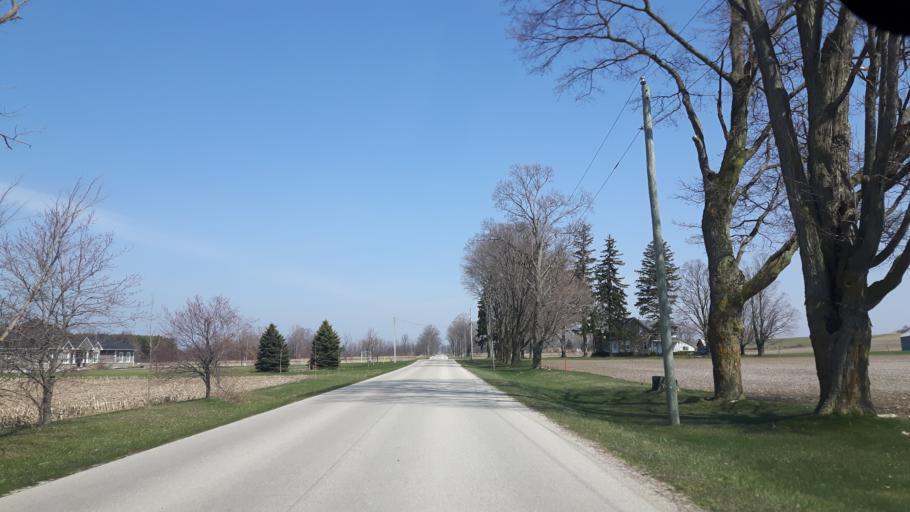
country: CA
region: Ontario
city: Goderich
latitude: 43.6732
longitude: -81.6847
